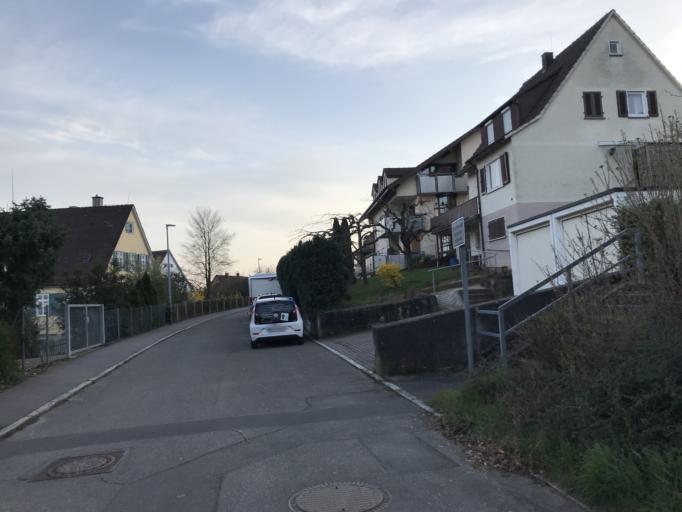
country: DE
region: Baden-Wuerttemberg
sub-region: Regierungsbezirk Stuttgart
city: Unterensingen
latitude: 48.6567
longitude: 9.3525
